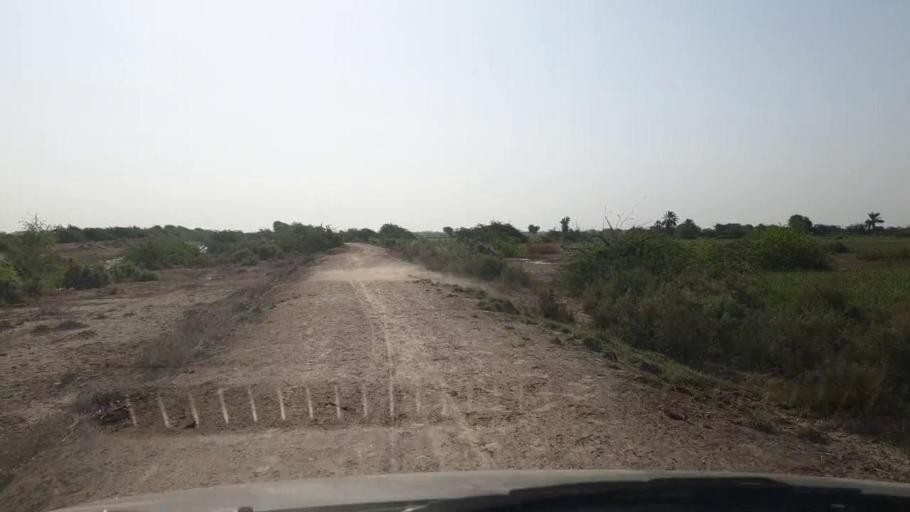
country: PK
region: Sindh
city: Kadhan
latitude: 24.5691
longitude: 69.0832
